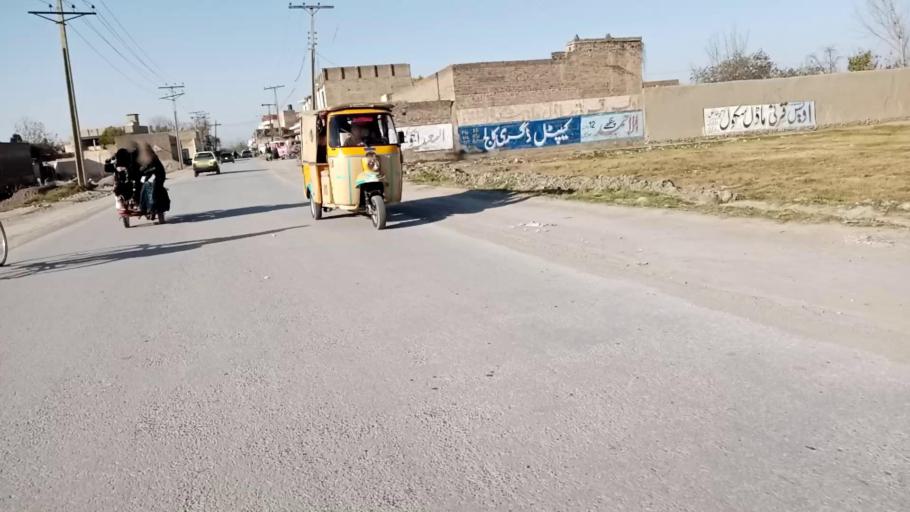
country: PK
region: Khyber Pakhtunkhwa
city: Peshawar
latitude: 34.0742
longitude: 71.5338
